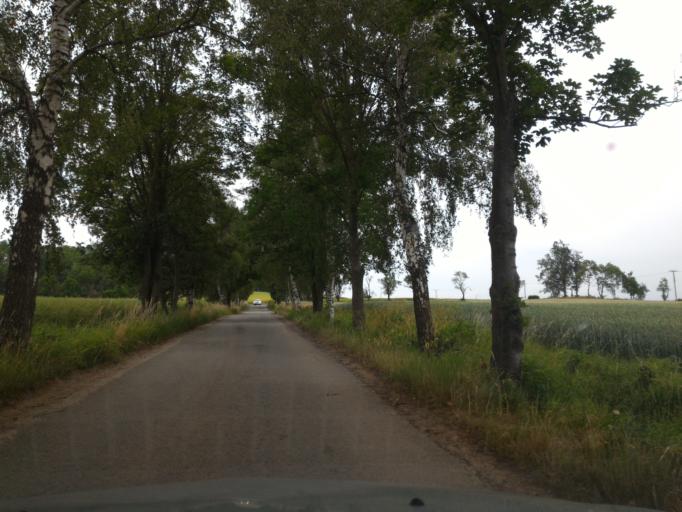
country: CZ
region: Vysocina
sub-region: Okres Jihlava
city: Telc
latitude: 49.1750
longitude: 15.4660
